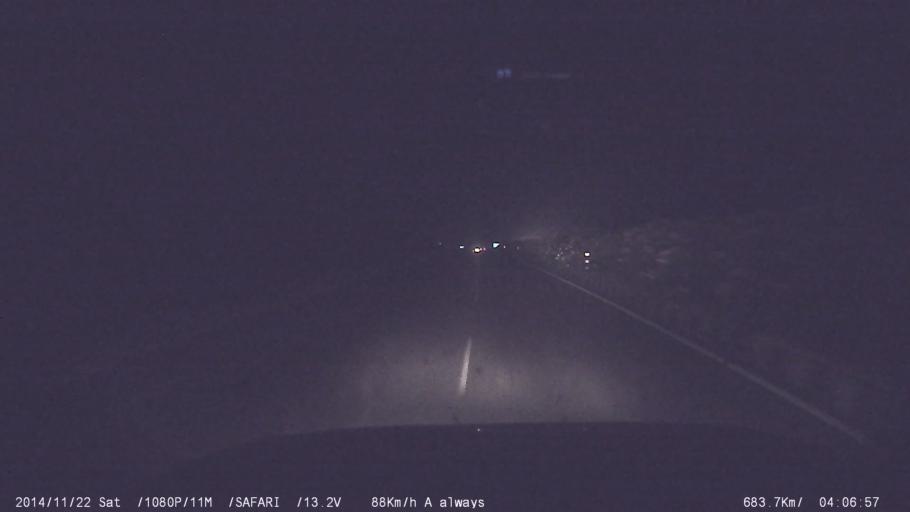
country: IN
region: Tamil Nadu
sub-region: Erode
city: Perundurai
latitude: 11.2905
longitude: 77.5701
